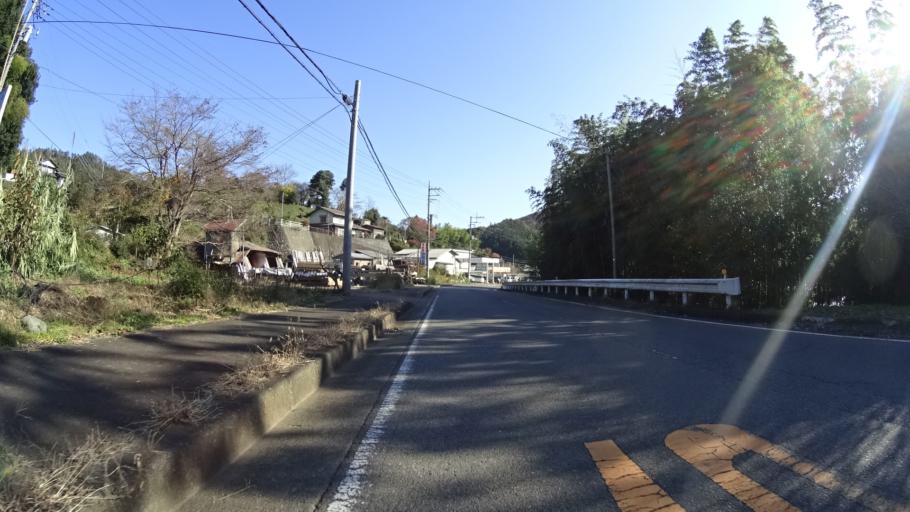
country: JP
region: Yamanashi
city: Uenohara
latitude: 35.6444
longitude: 139.1261
